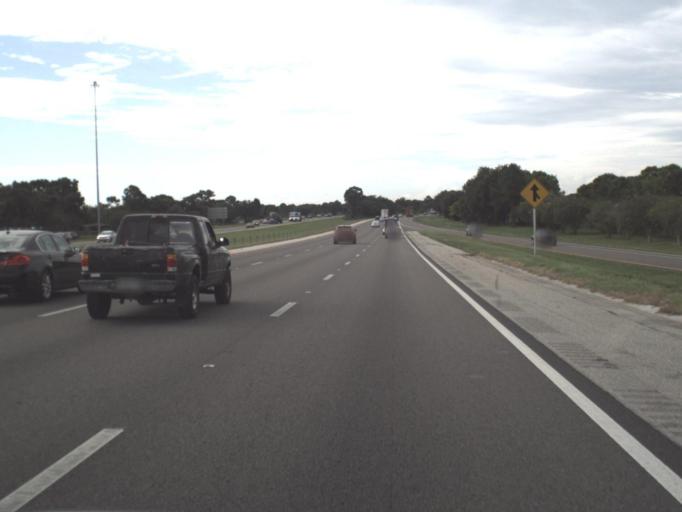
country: US
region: Florida
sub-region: Sarasota County
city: The Meadows
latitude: 27.3860
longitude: -82.4483
